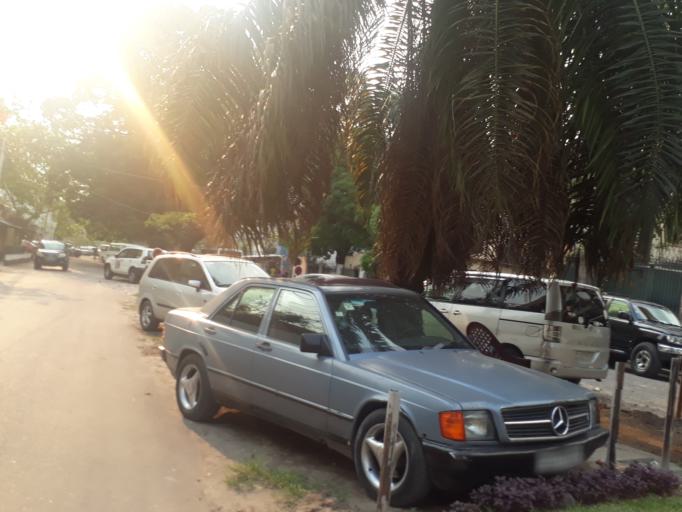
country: CD
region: Kinshasa
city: Kinshasa
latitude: -4.3008
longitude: 15.3129
